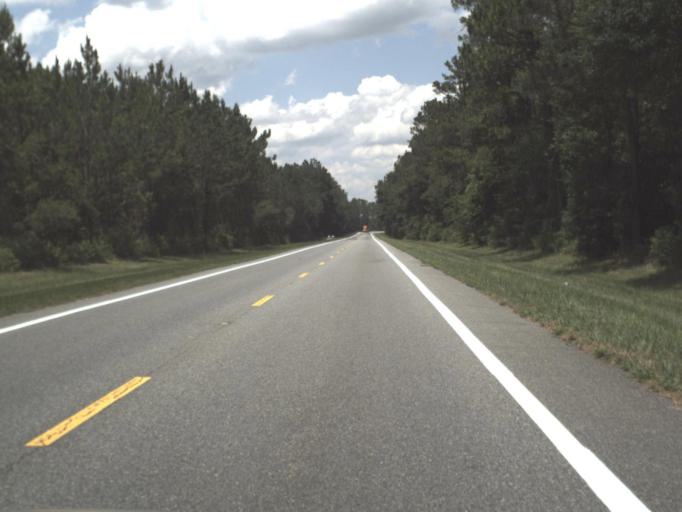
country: US
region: Florida
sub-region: Union County
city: Lake Butler
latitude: 30.1051
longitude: -82.2167
